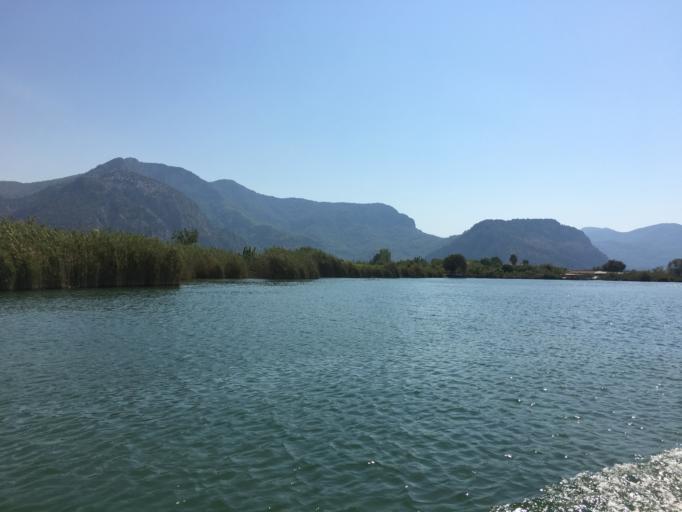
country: TR
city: Dalyan
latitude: 36.8206
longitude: 28.6355
